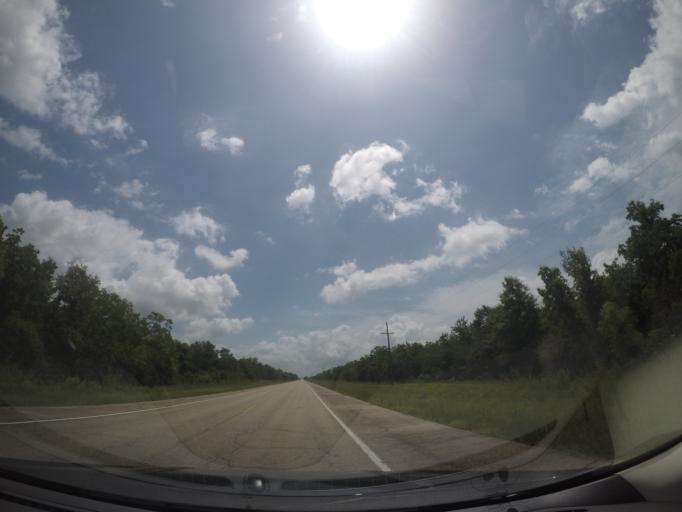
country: US
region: Mississippi
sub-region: Hancock County
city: Pearlington
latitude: 30.2334
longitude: -89.6533
